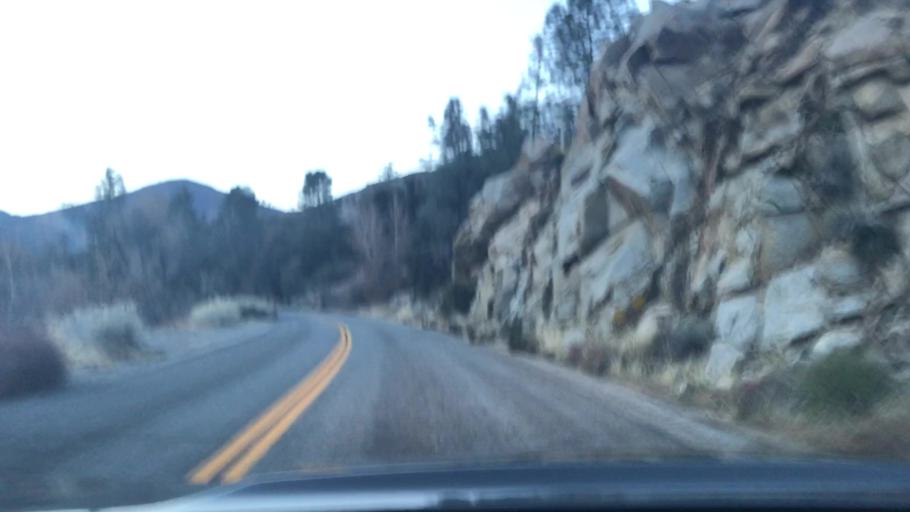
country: US
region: California
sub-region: Kern County
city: Kernville
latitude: 35.8994
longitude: -118.4680
